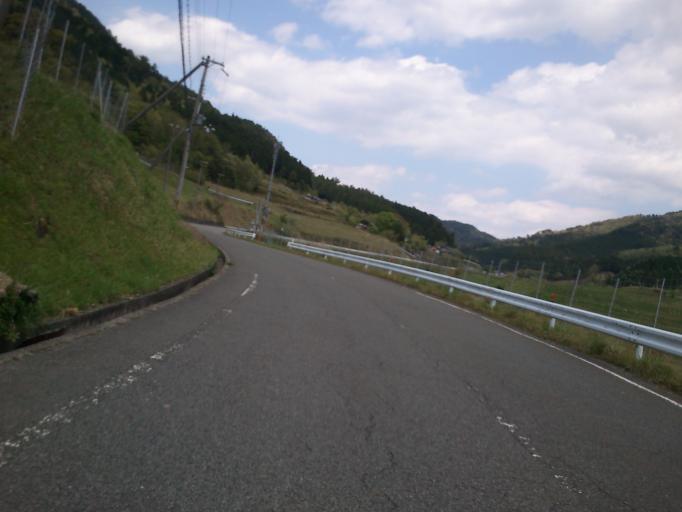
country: JP
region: Kyoto
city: Fukuchiyama
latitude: 35.3796
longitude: 134.9733
